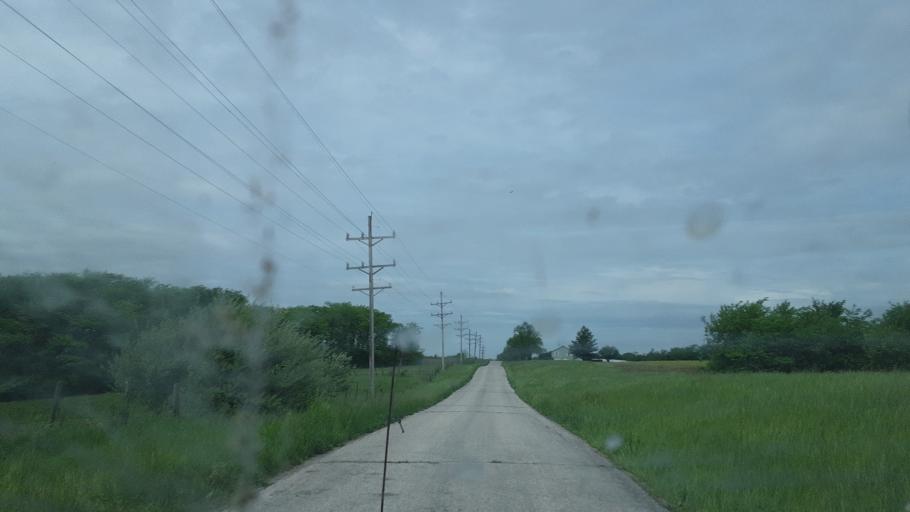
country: US
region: Missouri
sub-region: Clark County
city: Kahoka
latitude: 40.4238
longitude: -91.5924
